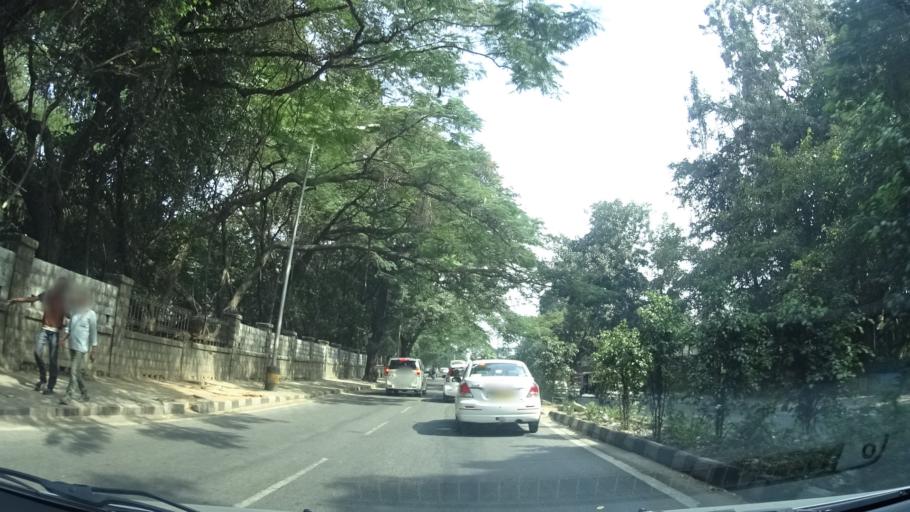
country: IN
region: Karnataka
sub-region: Bangalore Urban
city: Bangalore
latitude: 13.0157
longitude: 77.5633
